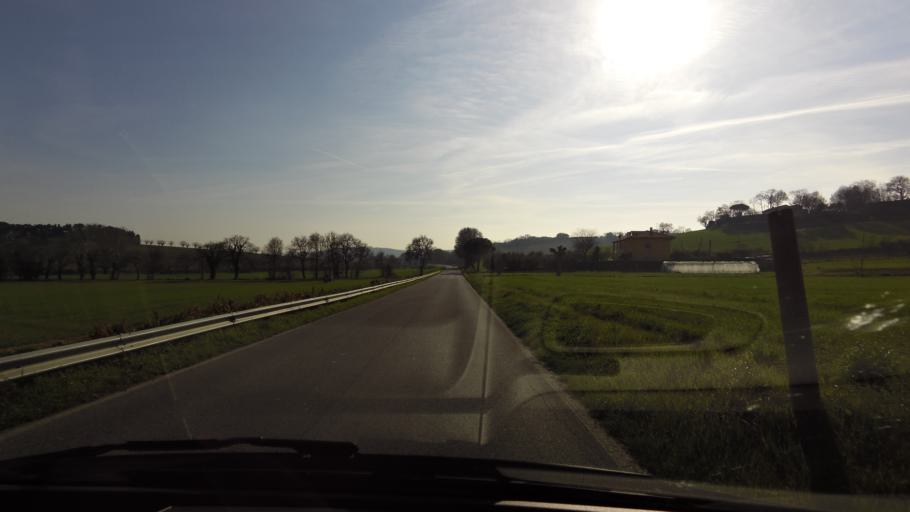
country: IT
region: The Marches
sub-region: Provincia di Ancona
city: Marcelli
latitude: 43.4886
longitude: 13.6105
